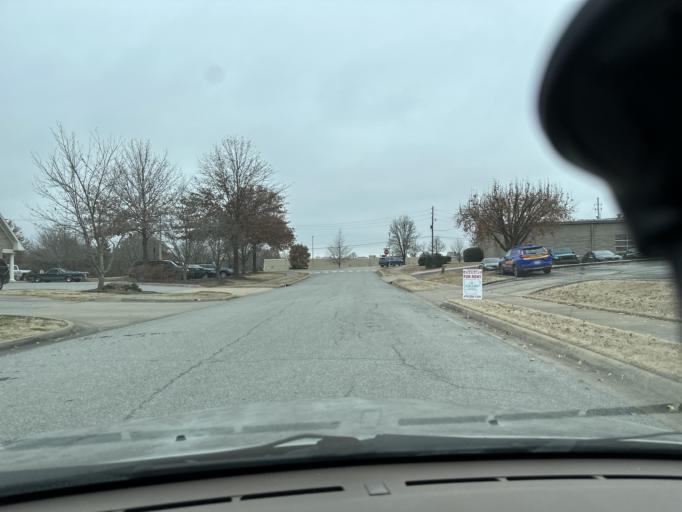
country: US
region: Arkansas
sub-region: Washington County
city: Johnson
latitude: 36.1046
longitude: -94.1492
